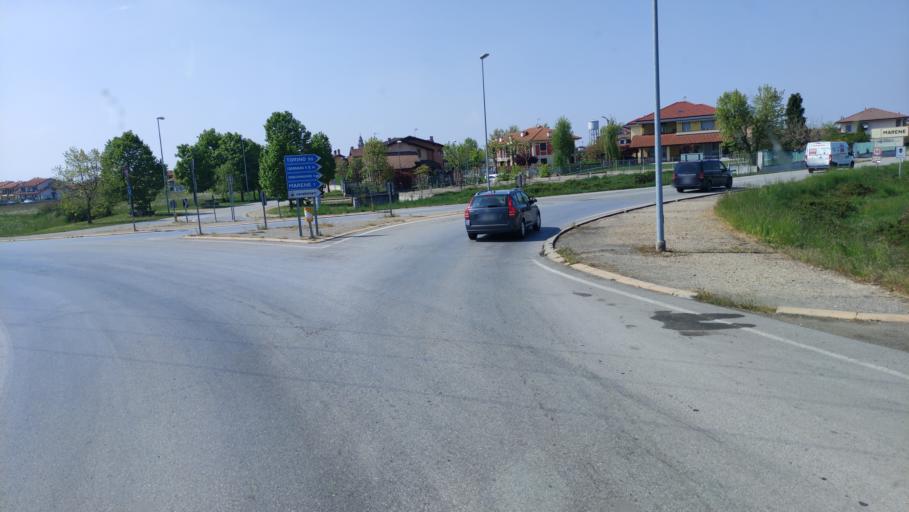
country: IT
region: Piedmont
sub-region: Provincia di Cuneo
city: Marene
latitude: 44.6581
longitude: 7.7389
